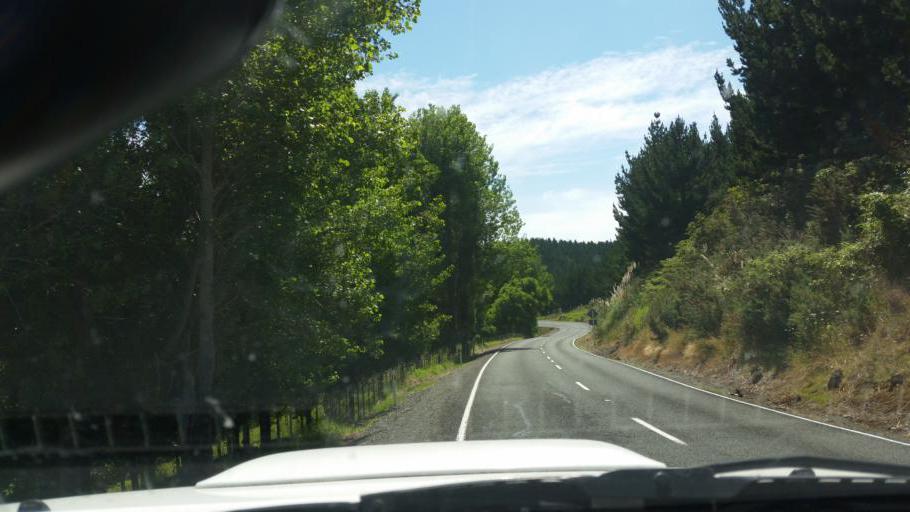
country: NZ
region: Auckland
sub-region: Auckland
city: Wellsford
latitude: -36.2039
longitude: 174.3940
